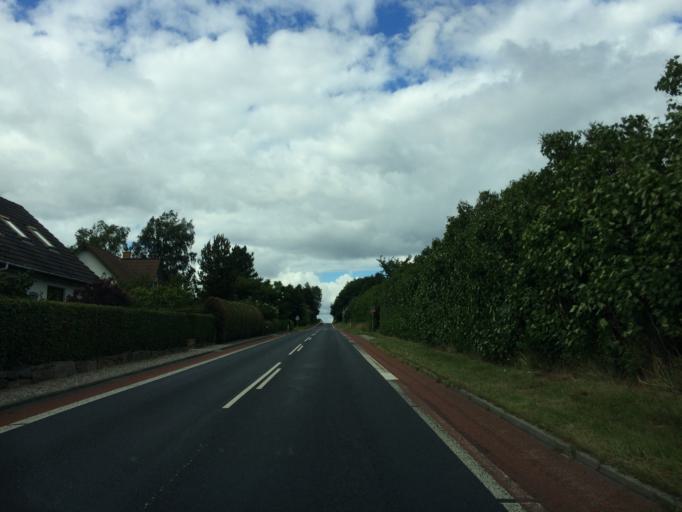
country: DK
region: South Denmark
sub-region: Assens Kommune
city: Harby
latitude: 55.1827
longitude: 10.1538
